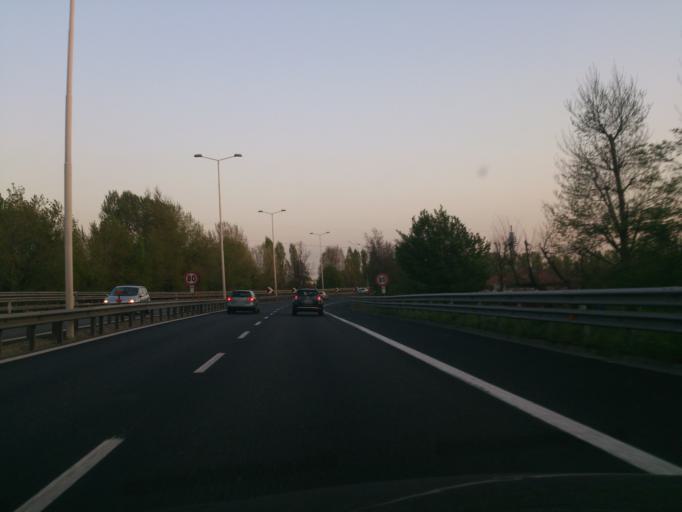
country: IT
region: Lombardy
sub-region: Citta metropolitana di Milano
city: Cologno Monzese
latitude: 45.5343
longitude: 9.2626
